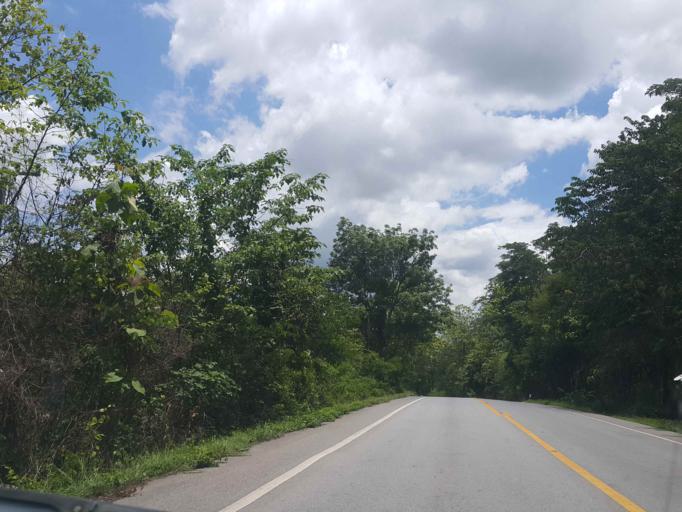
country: TH
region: Nan
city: Wiang Sa
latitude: 18.5262
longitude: 100.6179
